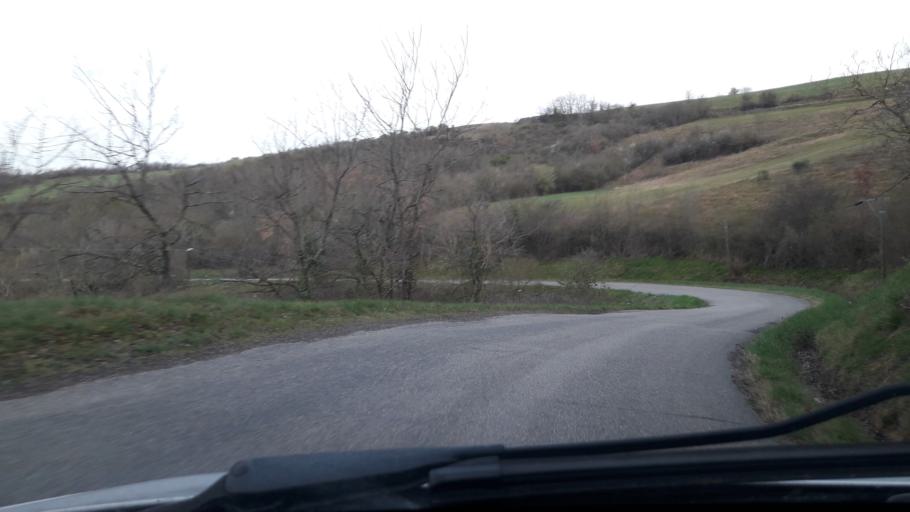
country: FR
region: Midi-Pyrenees
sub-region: Departement de la Haute-Garonne
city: Montesquieu-Volvestre
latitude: 43.1766
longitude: 1.2895
